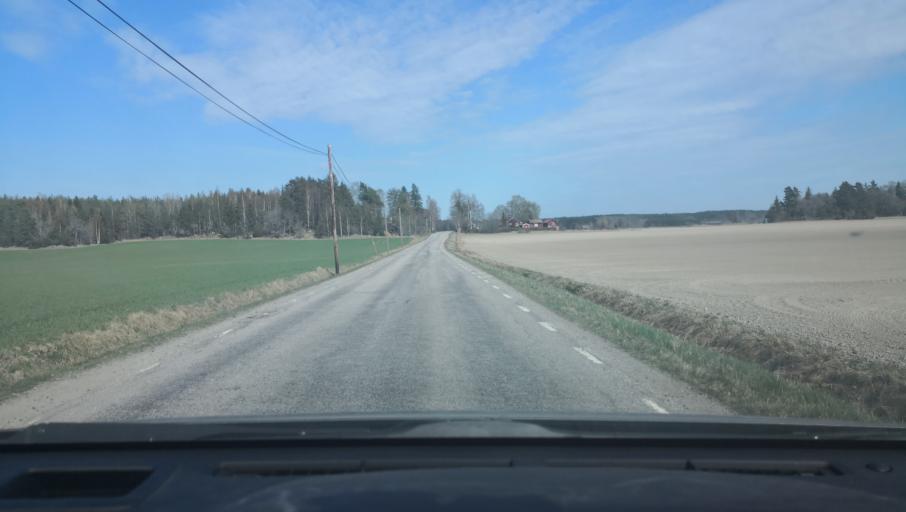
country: SE
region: Uppsala
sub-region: Enkopings Kommun
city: Irsta
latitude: 59.7790
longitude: 16.9425
